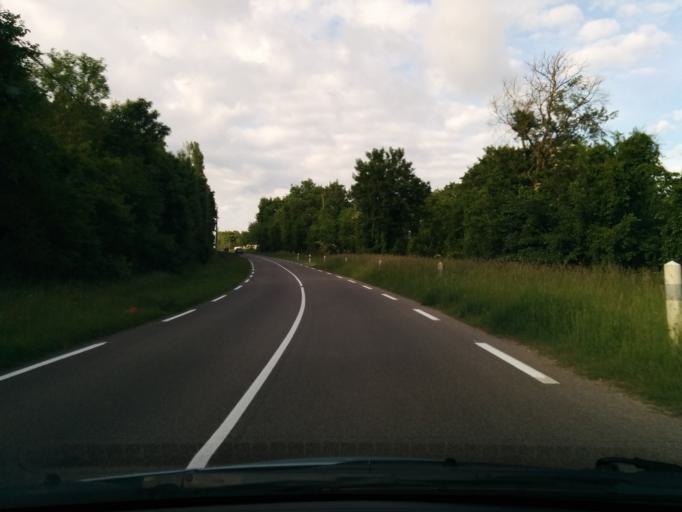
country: FR
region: Ile-de-France
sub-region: Departement des Yvelines
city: Follainville-Dennemont
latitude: 49.0490
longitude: 1.6919
